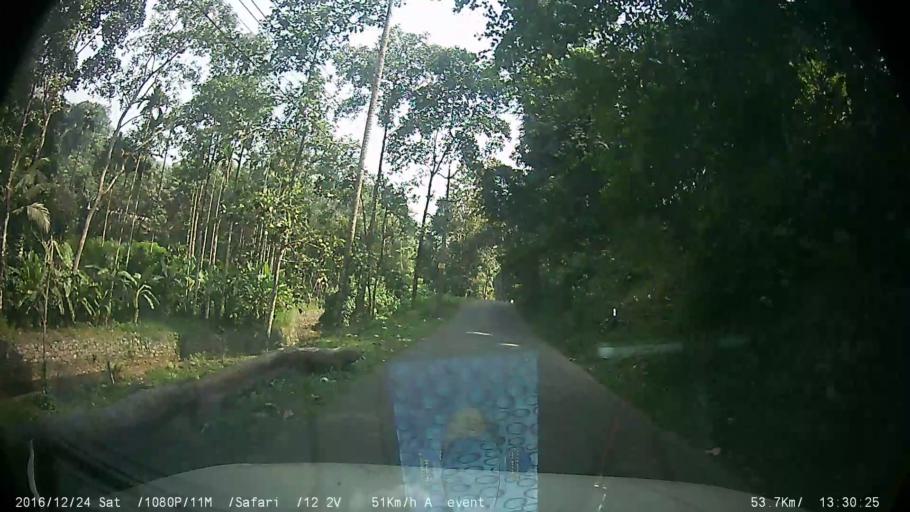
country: IN
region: Kerala
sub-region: Kottayam
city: Palackattumala
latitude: 9.8478
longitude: 76.7017
